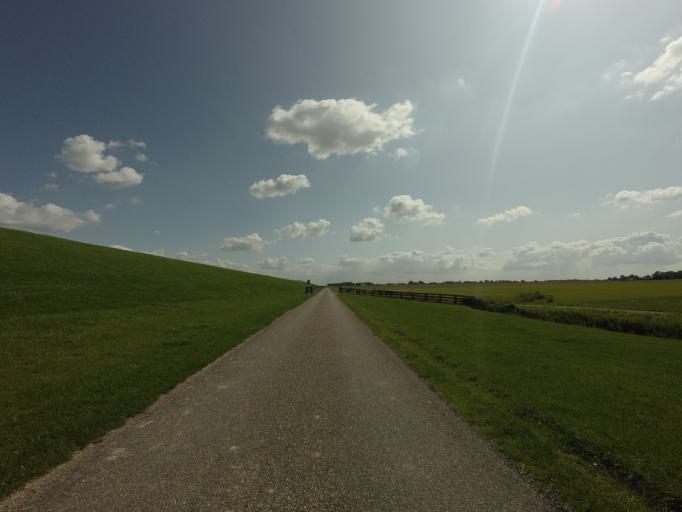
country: NL
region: Friesland
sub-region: Gemeente Ferwerderadiel
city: Hallum
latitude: 53.3218
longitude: 5.7446
